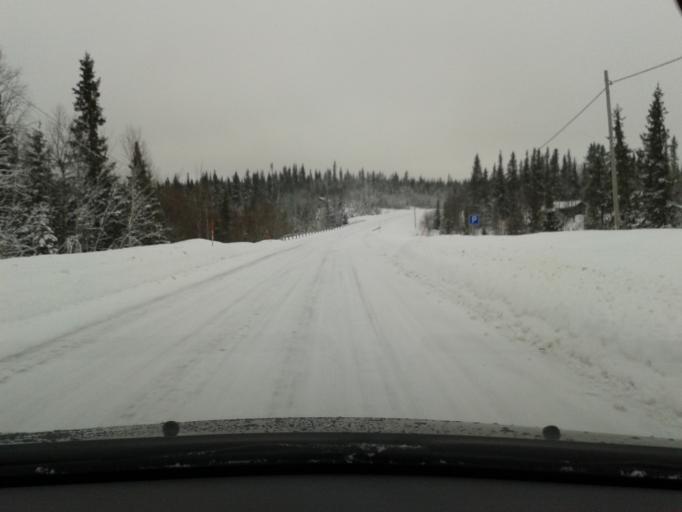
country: SE
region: Vaesterbotten
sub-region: Vilhelmina Kommun
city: Sjoberg
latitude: 65.1651
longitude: 15.8801
